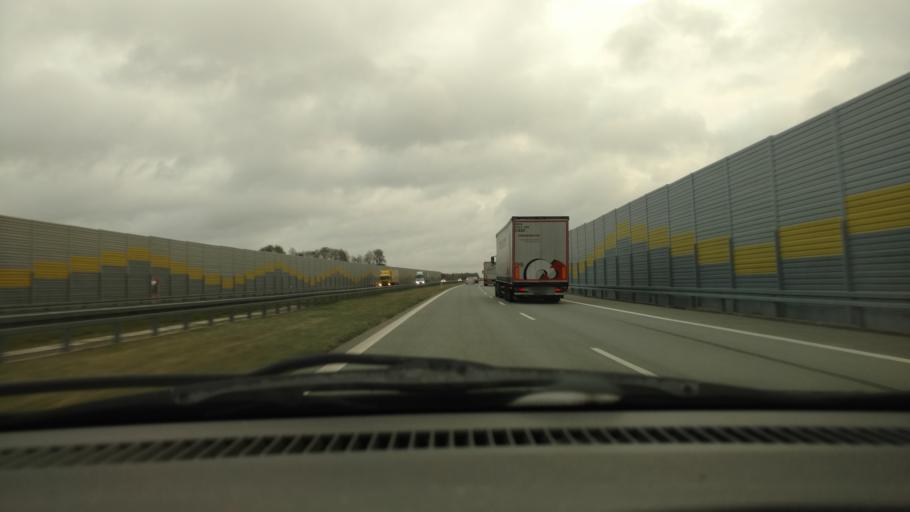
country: PL
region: Lodz Voivodeship
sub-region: Powiat pabianicki
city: Ksawerow
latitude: 51.6295
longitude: 19.4076
